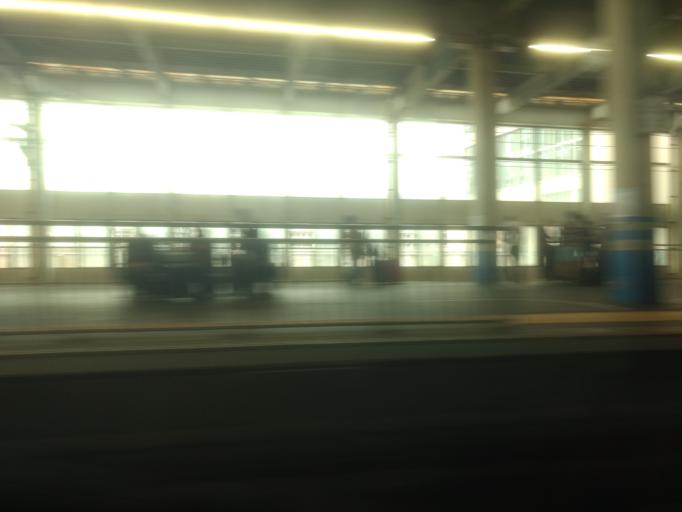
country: JP
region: Hiroshima
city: Hiroshima-shi
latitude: 34.3979
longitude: 132.4764
